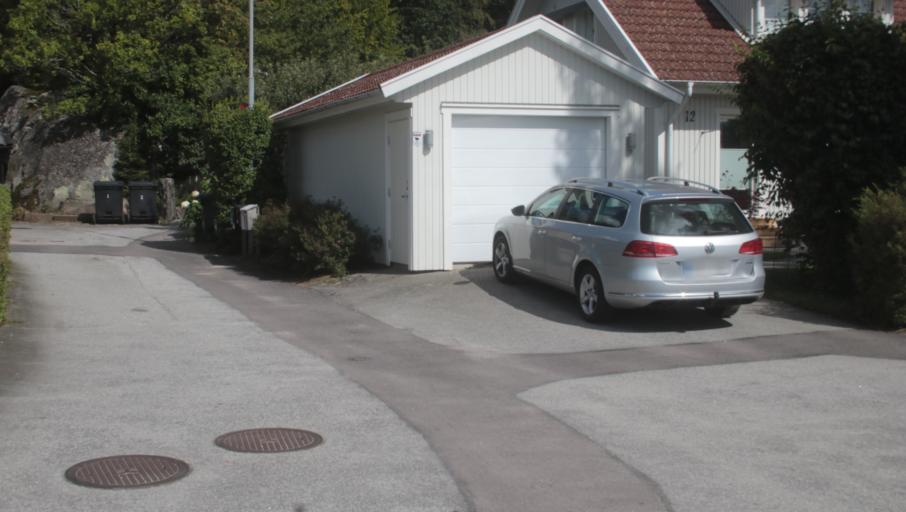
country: SE
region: Blekinge
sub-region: Karlshamns Kommun
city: Karlshamn
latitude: 56.1874
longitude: 14.8601
